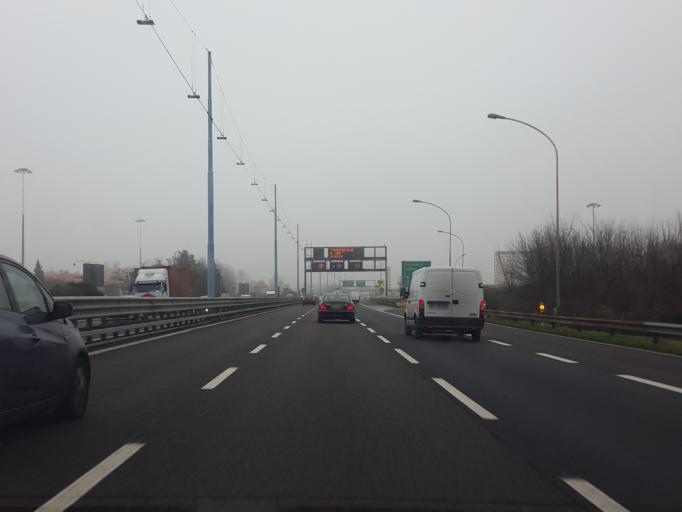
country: IT
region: Veneto
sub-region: Provincia di Treviso
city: Mogliano Veneto
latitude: 45.5246
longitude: 12.2594
